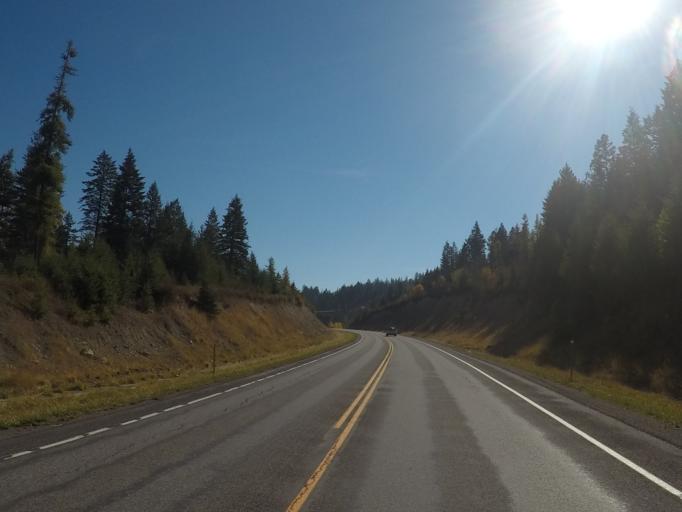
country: US
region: Montana
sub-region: Flathead County
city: Lakeside
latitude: 47.9932
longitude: -114.2088
